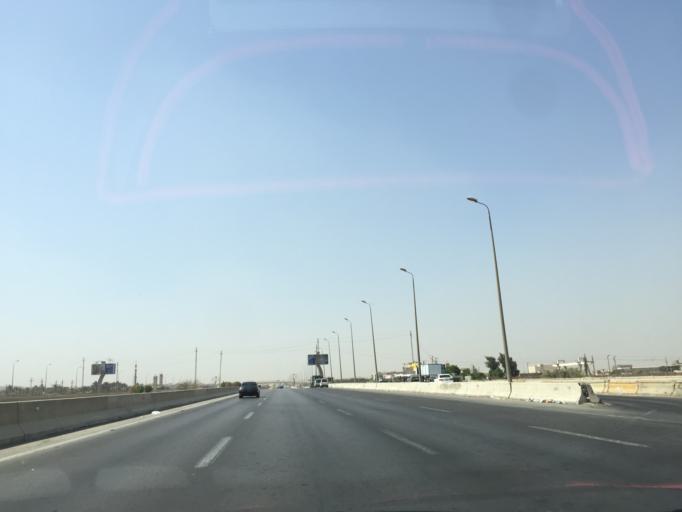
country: EG
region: Al Jizah
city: Awsim
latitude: 30.0728
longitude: 31.0096
